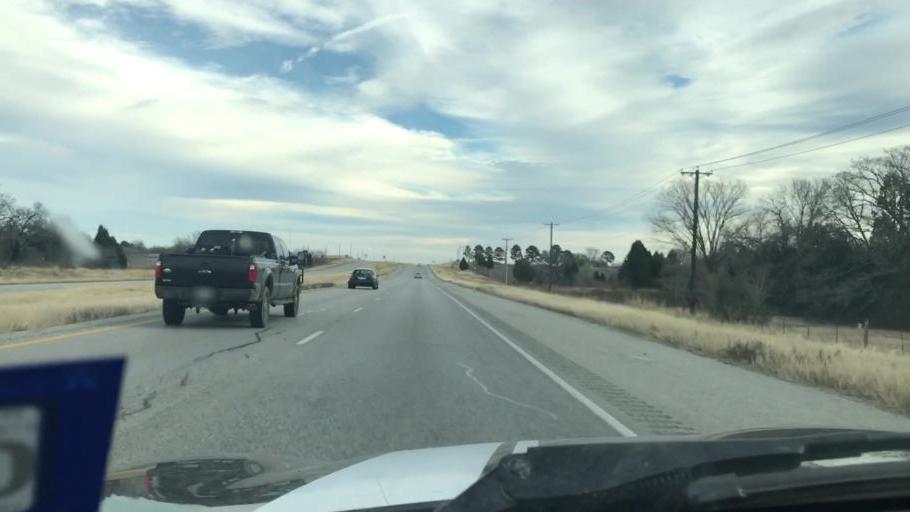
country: US
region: Texas
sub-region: Bastrop County
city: Elgin
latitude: 30.3174
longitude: -97.3138
